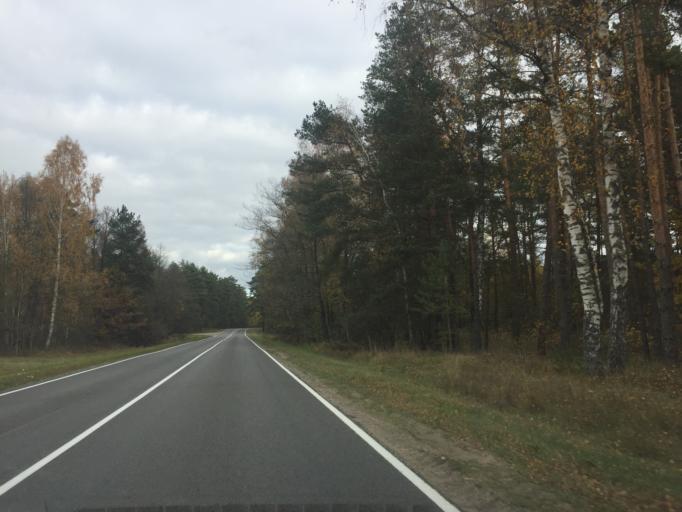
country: BY
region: Minsk
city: Svir
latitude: 54.8818
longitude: 26.3708
